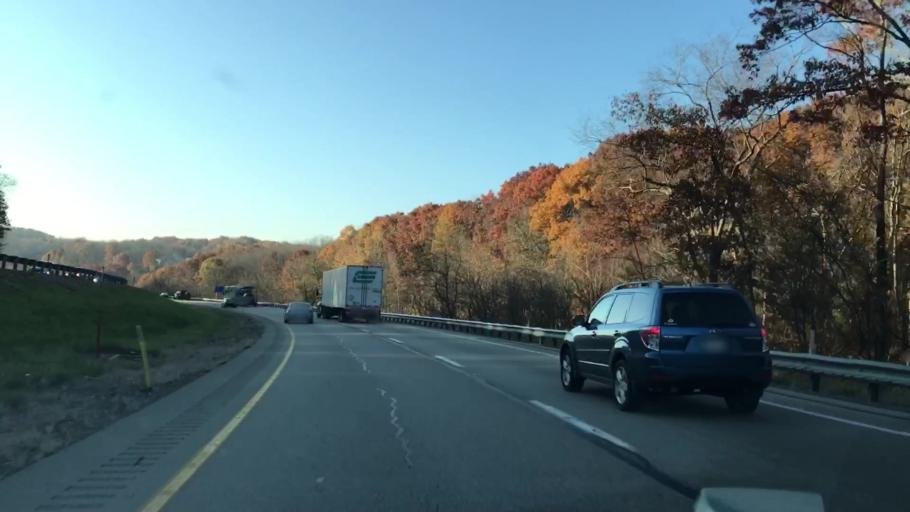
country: US
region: Pennsylvania
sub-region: Allegheny County
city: Franklin Park
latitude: 40.5784
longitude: -80.1172
